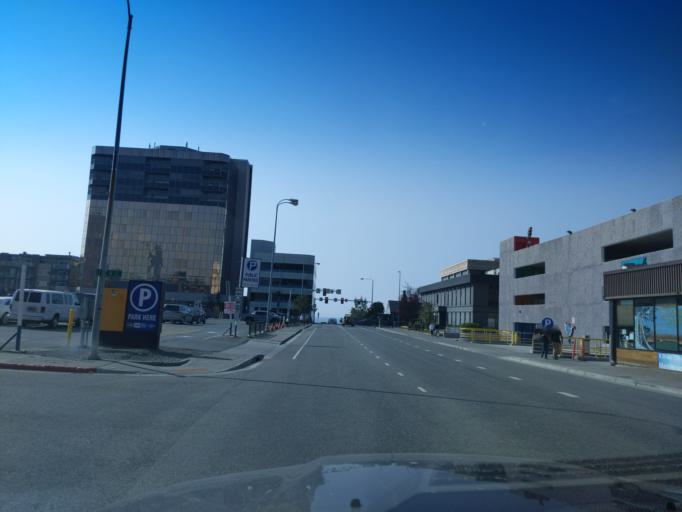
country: US
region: Alaska
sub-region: Anchorage Municipality
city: Anchorage
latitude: 61.2176
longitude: -149.9015
